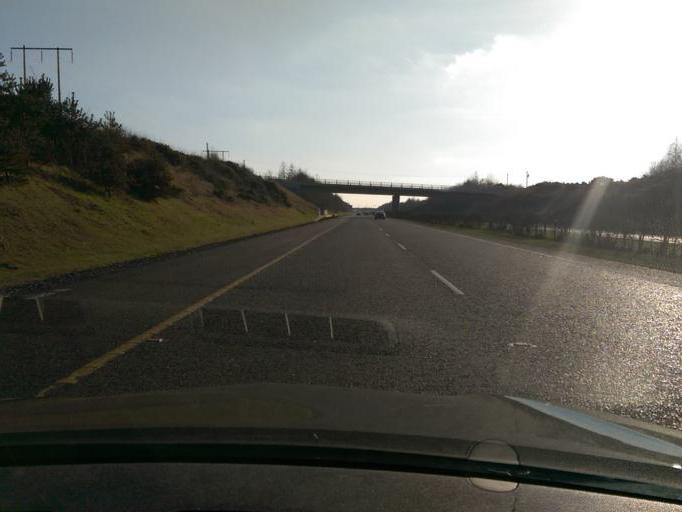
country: IE
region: Leinster
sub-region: Laois
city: Stradbally
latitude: 53.0678
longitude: -7.2153
